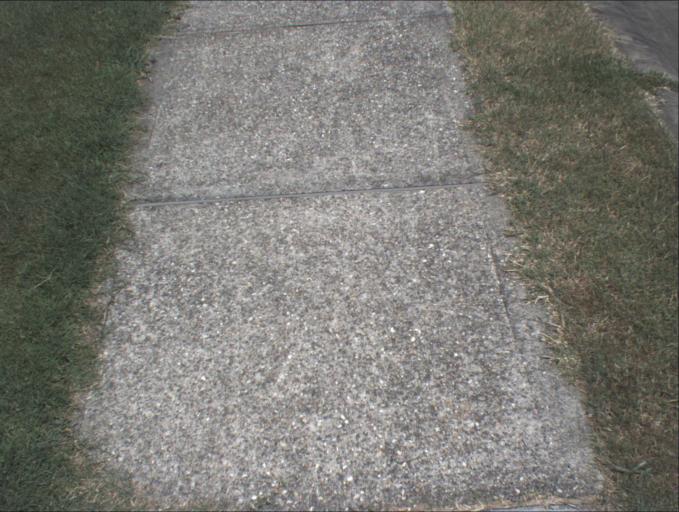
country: AU
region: Queensland
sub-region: Logan
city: Windaroo
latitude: -27.7382
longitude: 153.1867
